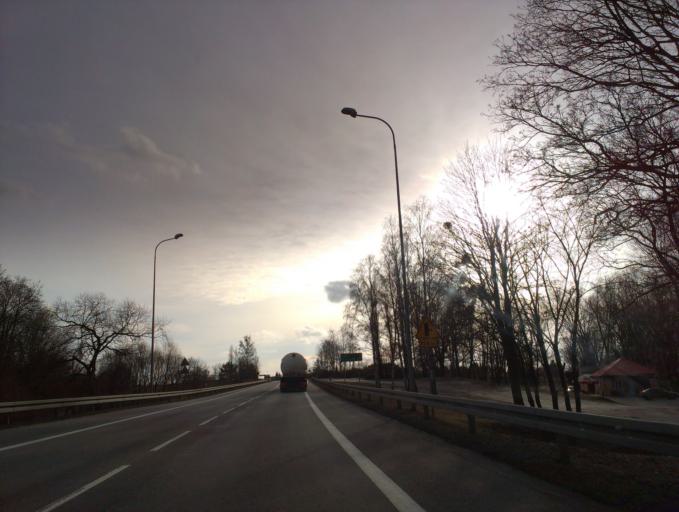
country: PL
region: Kujawsko-Pomorskie
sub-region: Powiat lipnowski
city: Kikol
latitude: 52.9079
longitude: 19.1202
